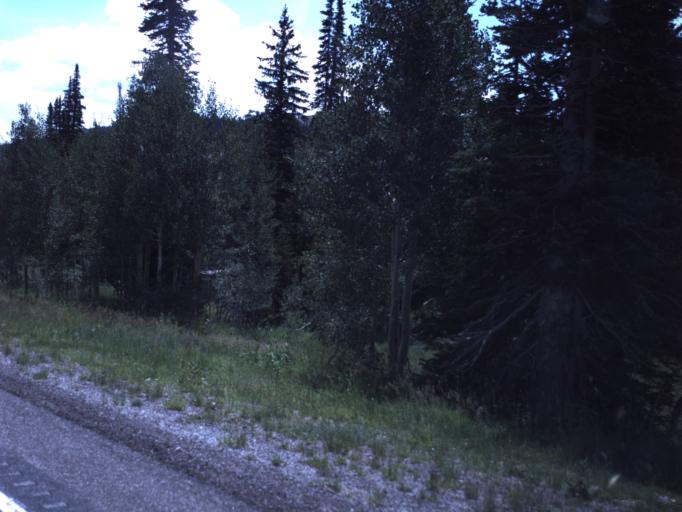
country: US
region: Utah
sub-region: Sanpete County
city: Fairview
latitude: 39.5999
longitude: -111.2723
